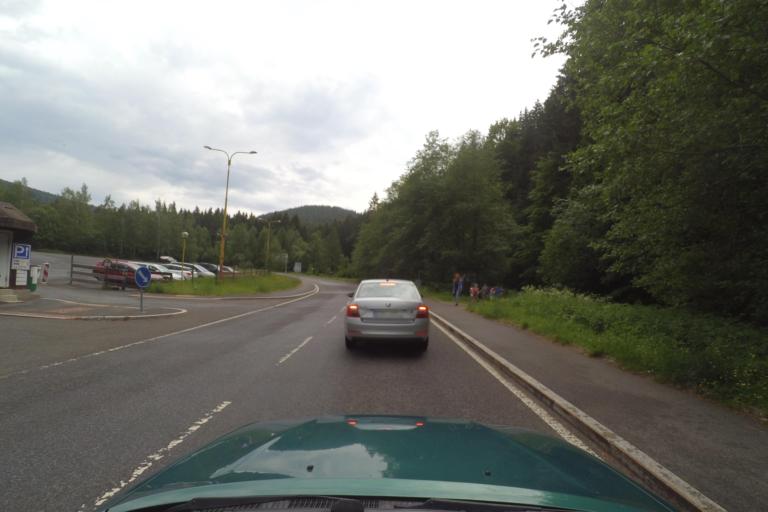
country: CZ
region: Liberecky
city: Harrachov
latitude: 50.7688
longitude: 15.4386
